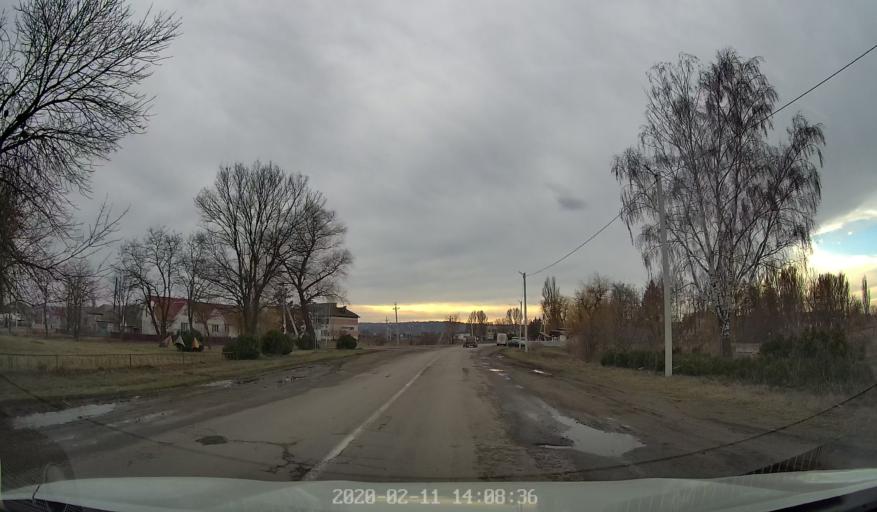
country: RO
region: Botosani
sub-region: Comuna Darabani
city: Bajura
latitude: 48.2356
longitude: 26.5461
